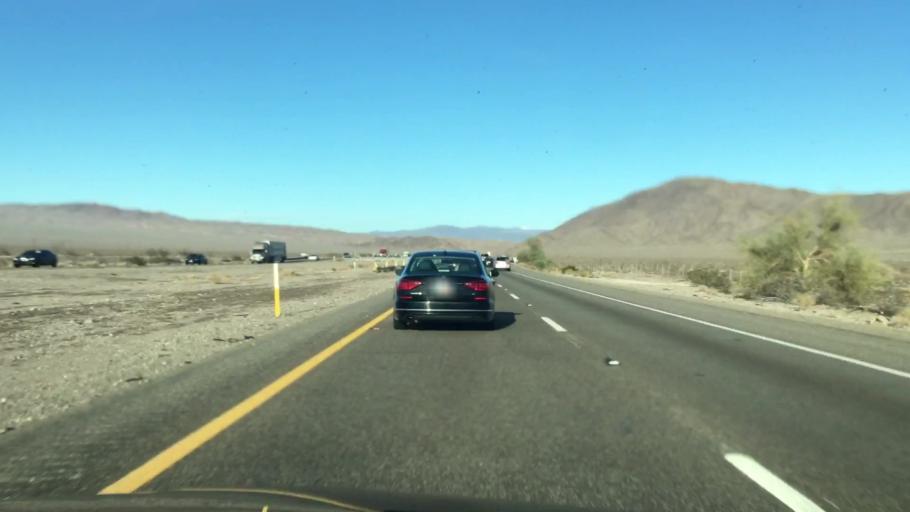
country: US
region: California
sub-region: San Bernardino County
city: Fort Irwin
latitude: 35.1638
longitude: -116.1851
